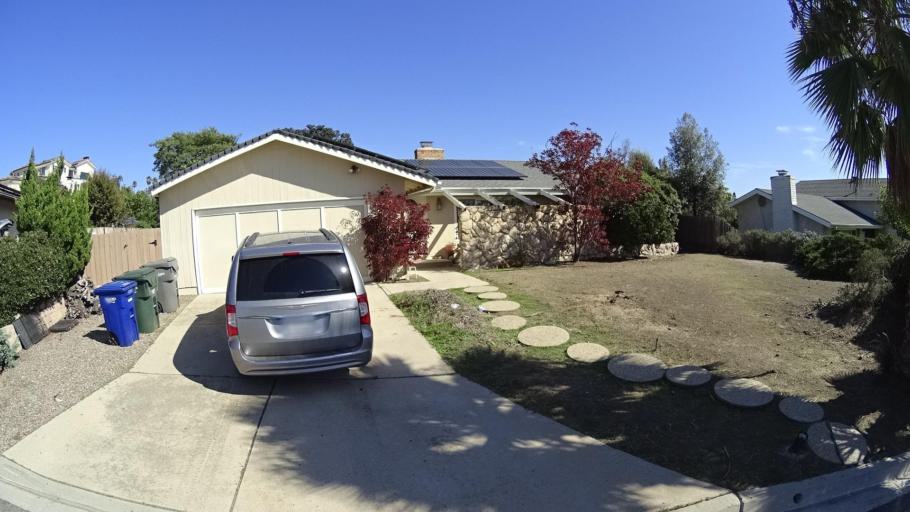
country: US
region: California
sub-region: San Diego County
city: Casa de Oro-Mount Helix
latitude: 32.7583
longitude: -116.9811
